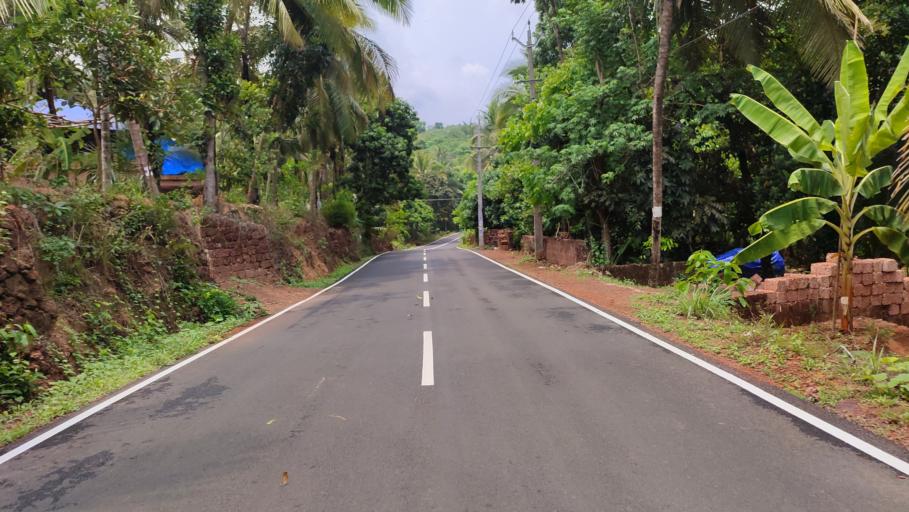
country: IN
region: Kerala
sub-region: Kasaragod District
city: Kannangad
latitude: 12.3187
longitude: 75.1494
